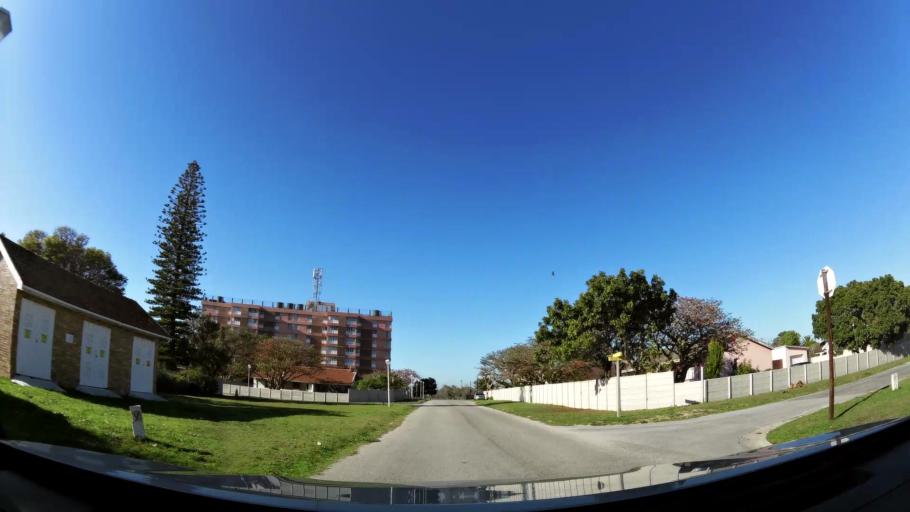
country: ZA
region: Eastern Cape
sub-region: Nelson Mandela Bay Metropolitan Municipality
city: Port Elizabeth
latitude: -33.9884
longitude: 25.6283
